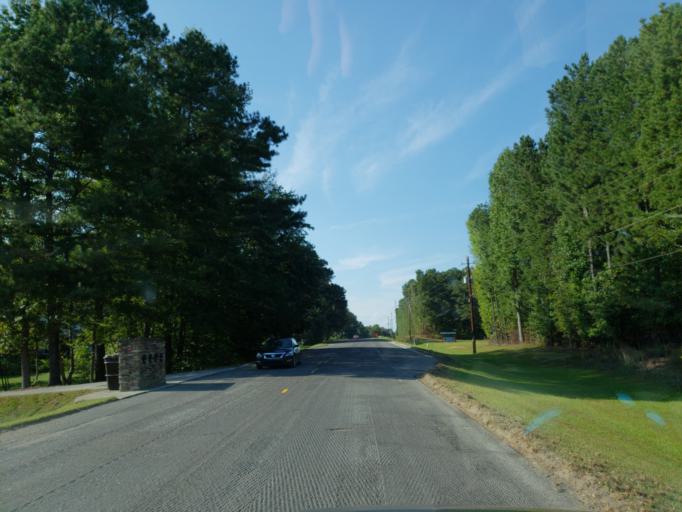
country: US
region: Georgia
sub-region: Cobb County
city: Powder Springs
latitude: 33.8751
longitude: -84.7161
